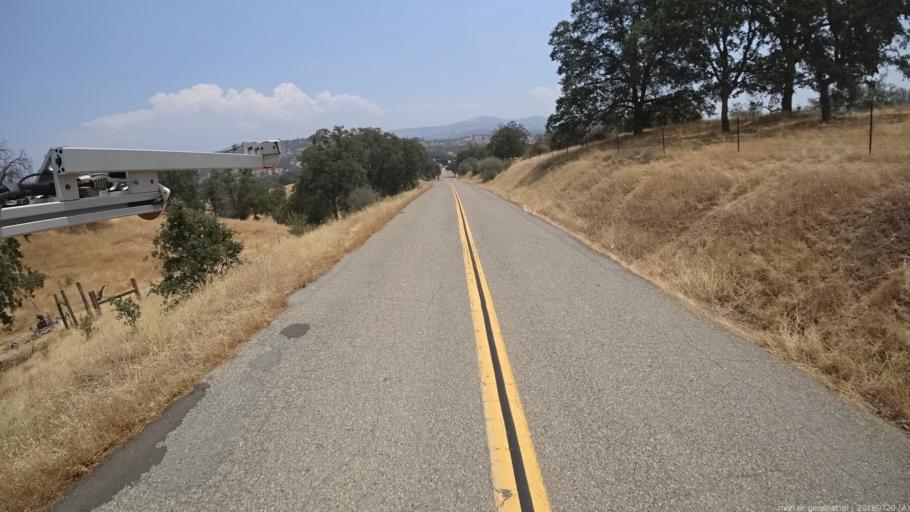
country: US
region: California
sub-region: Madera County
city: Yosemite Lakes
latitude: 37.2878
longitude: -119.8032
